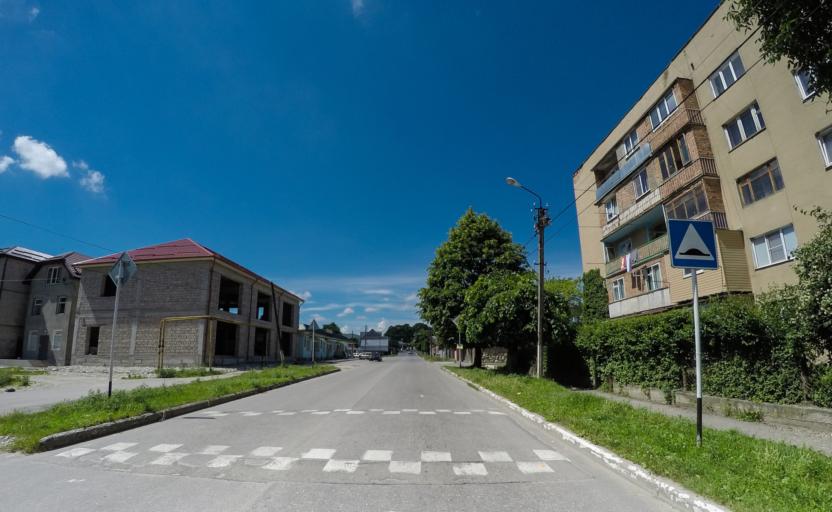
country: RU
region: Kabardino-Balkariya
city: Belaya Rechka
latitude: 43.4448
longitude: 43.5852
